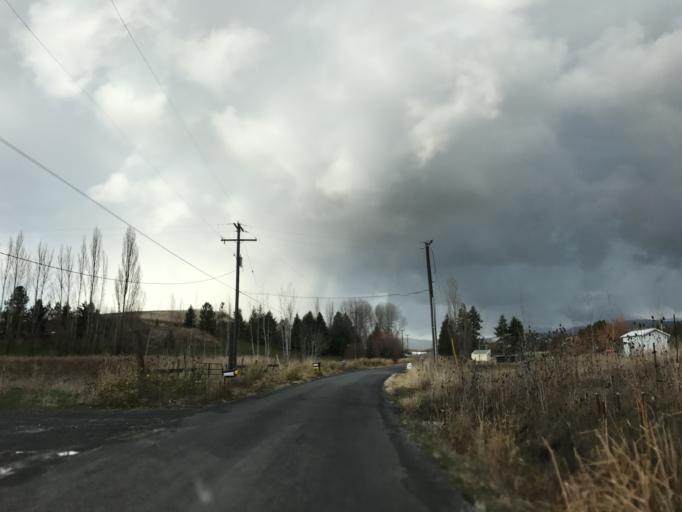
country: US
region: Idaho
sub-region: Latah County
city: Moscow
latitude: 46.7527
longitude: -116.9960
